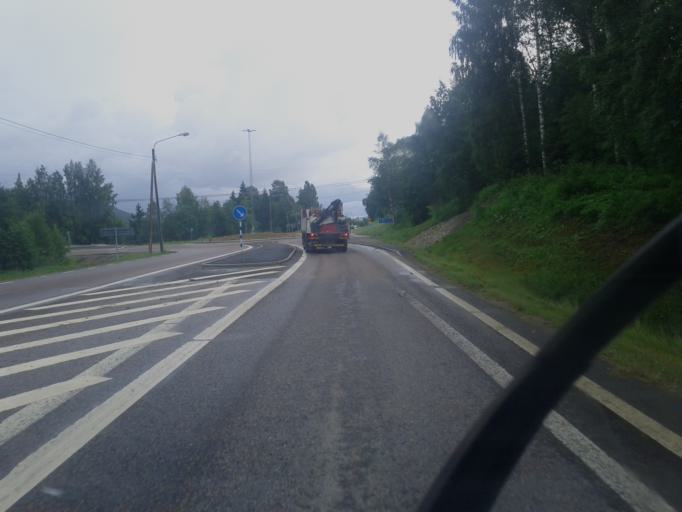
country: SE
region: Vaesternorrland
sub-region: Sundsvalls Kommun
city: Sundsvall
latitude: 62.3990
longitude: 17.2401
